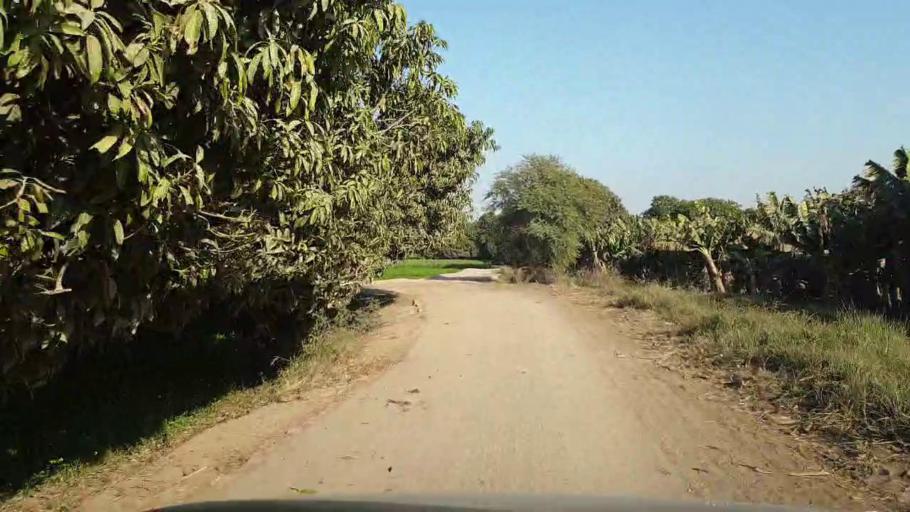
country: PK
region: Sindh
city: Tando Allahyar
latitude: 25.3532
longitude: 68.6836
